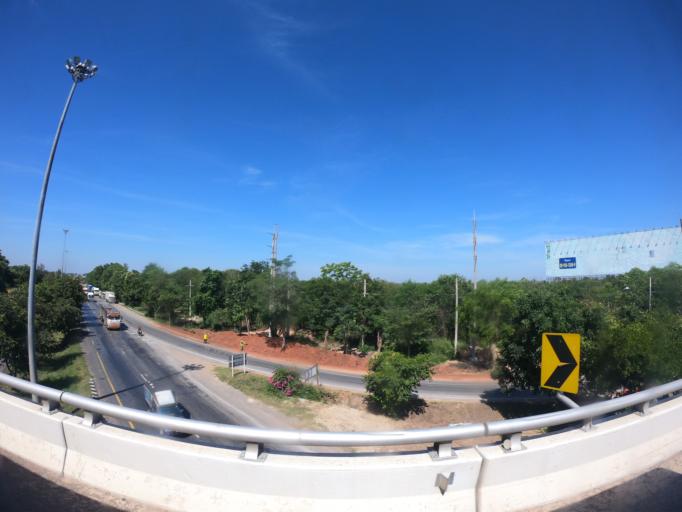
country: TH
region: Nakhon Ratchasima
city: Nakhon Ratchasima
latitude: 15.0561
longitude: 102.1576
